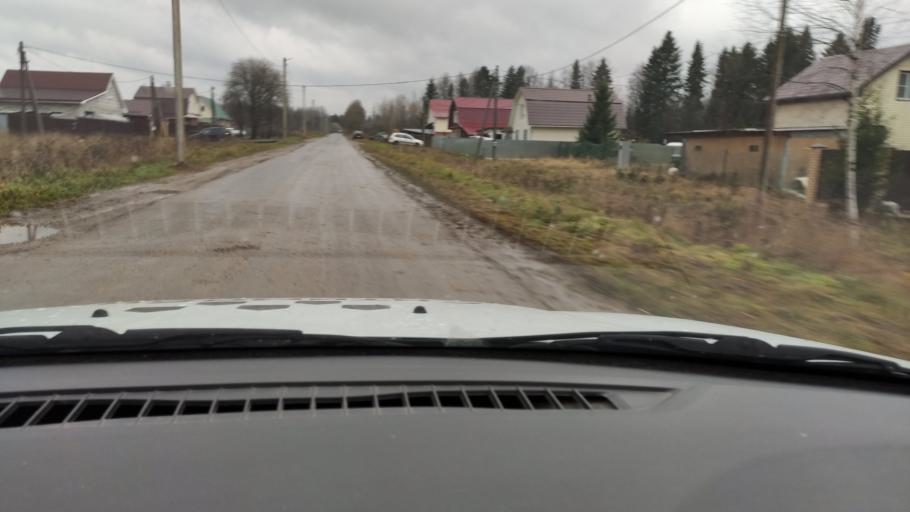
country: RU
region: Perm
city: Sylva
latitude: 58.0384
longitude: 56.7439
